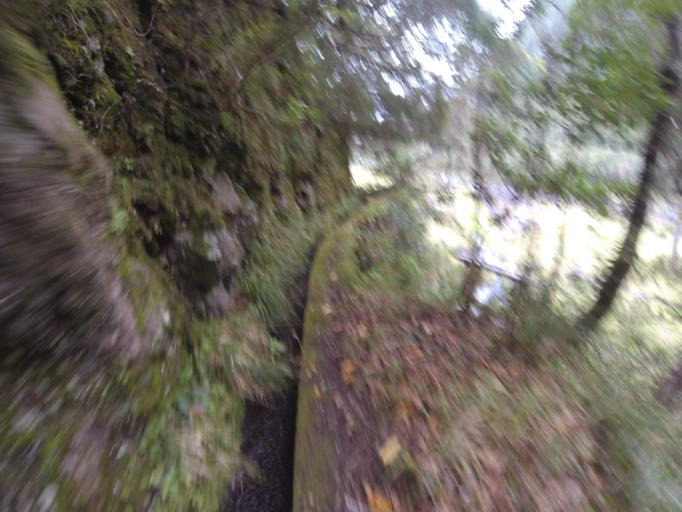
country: PT
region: Madeira
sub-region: Sao Vicente
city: Sao Vicente
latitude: 32.7941
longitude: -17.1133
